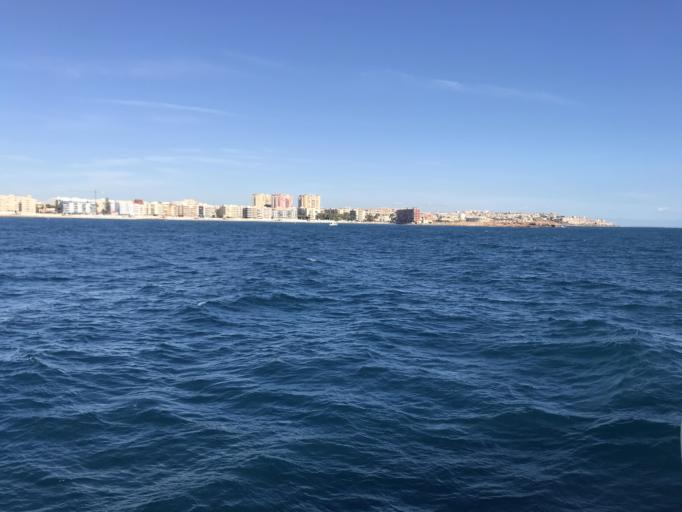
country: ES
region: Valencia
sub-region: Provincia de Alicante
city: Torrevieja
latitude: 37.9754
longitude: -0.6570
